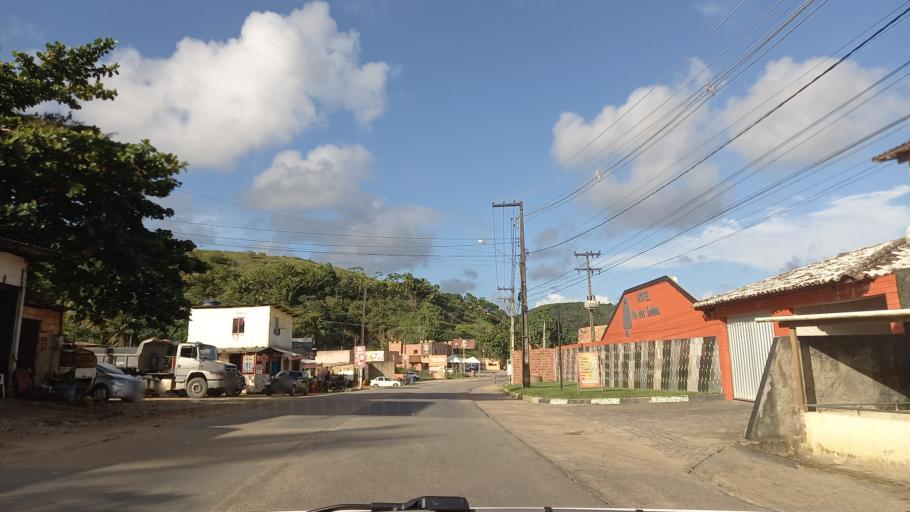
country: BR
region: Pernambuco
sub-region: Rio Formoso
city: Rio Formoso
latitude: -8.6573
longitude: -35.1545
